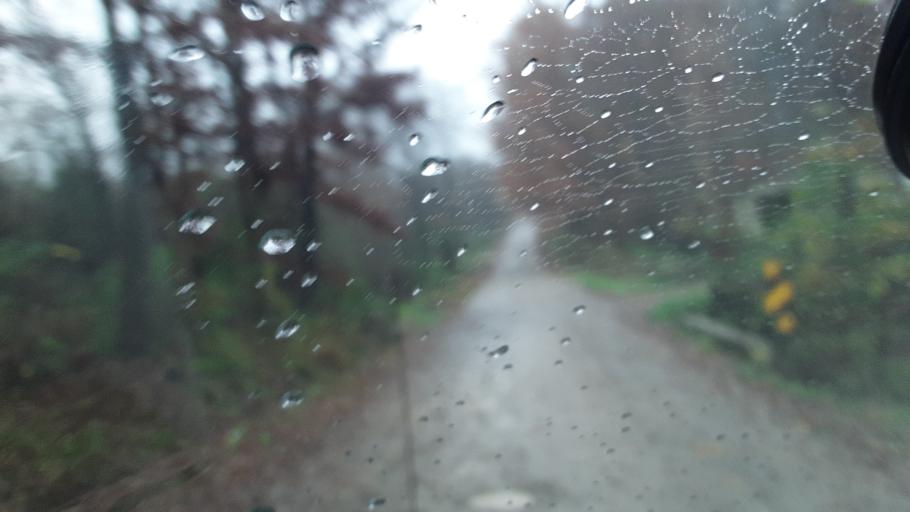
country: US
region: Ohio
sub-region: Vinton County
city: McArthur
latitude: 39.2251
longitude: -82.4632
